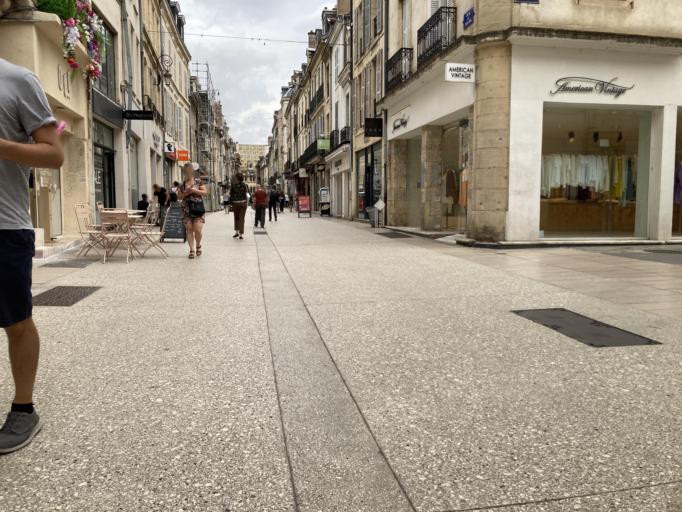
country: FR
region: Bourgogne
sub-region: Departement de la Cote-d'Or
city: Dijon
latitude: 47.3205
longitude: 5.0390
